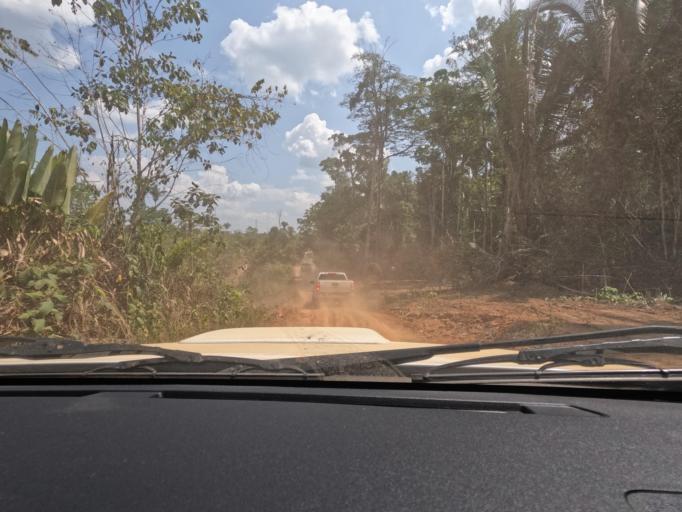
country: BR
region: Rondonia
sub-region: Porto Velho
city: Porto Velho
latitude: -8.6057
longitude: -64.2204
